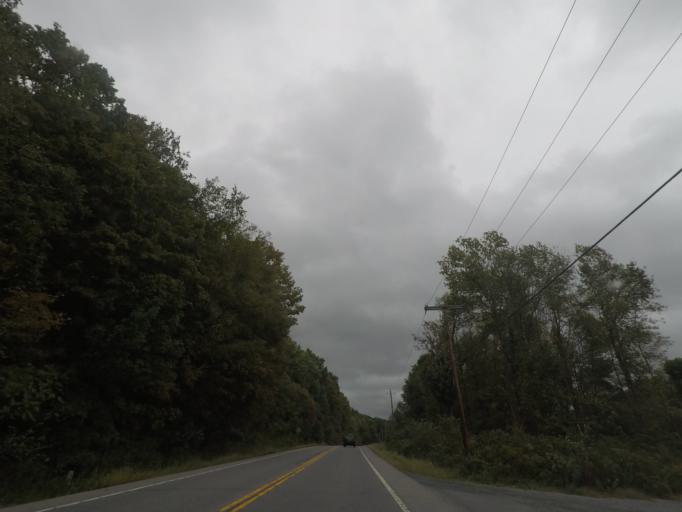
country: US
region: New York
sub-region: Saratoga County
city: Country Knolls
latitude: 42.9226
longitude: -73.7455
